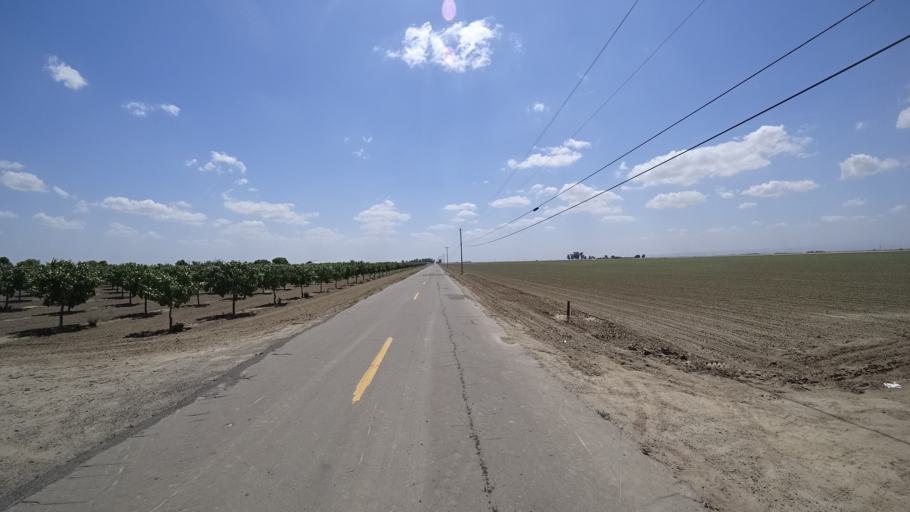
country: US
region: California
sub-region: Kings County
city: Stratford
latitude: 36.1784
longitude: -119.8161
